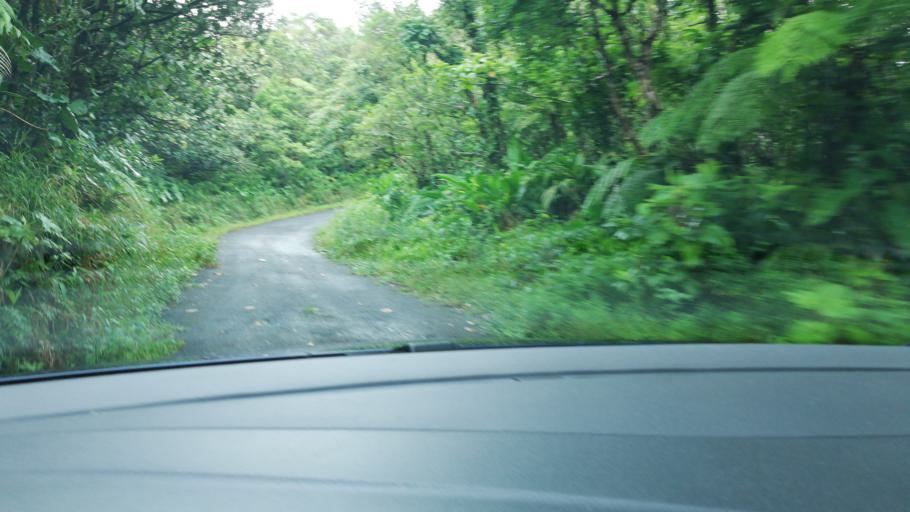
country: GP
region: Guadeloupe
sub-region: Guadeloupe
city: Saint-Claude
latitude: 16.0363
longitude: -61.6694
